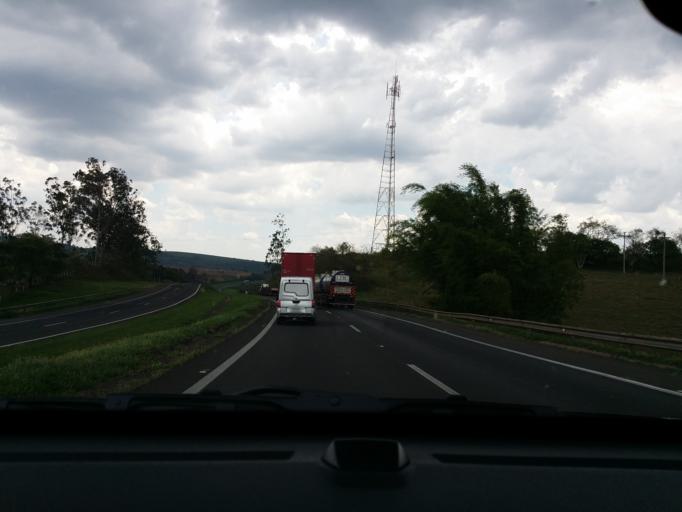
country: BR
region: Sao Paulo
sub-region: Rio Claro
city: Rio Claro
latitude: -22.3030
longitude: -47.6698
